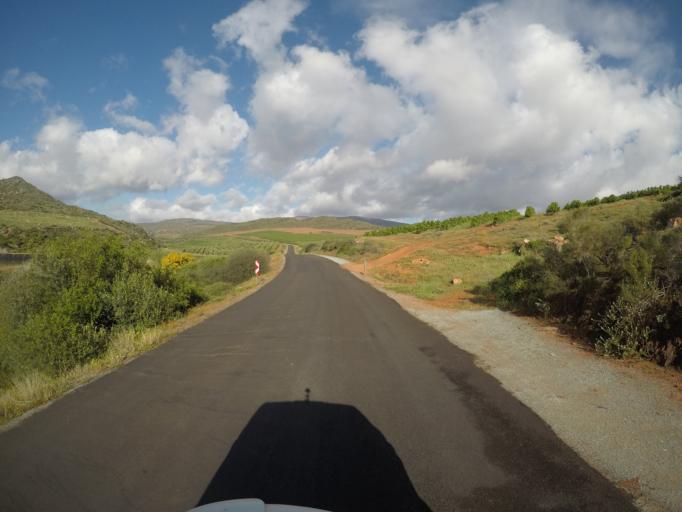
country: ZA
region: Western Cape
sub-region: West Coast District Municipality
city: Clanwilliam
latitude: -32.4302
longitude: 18.9529
